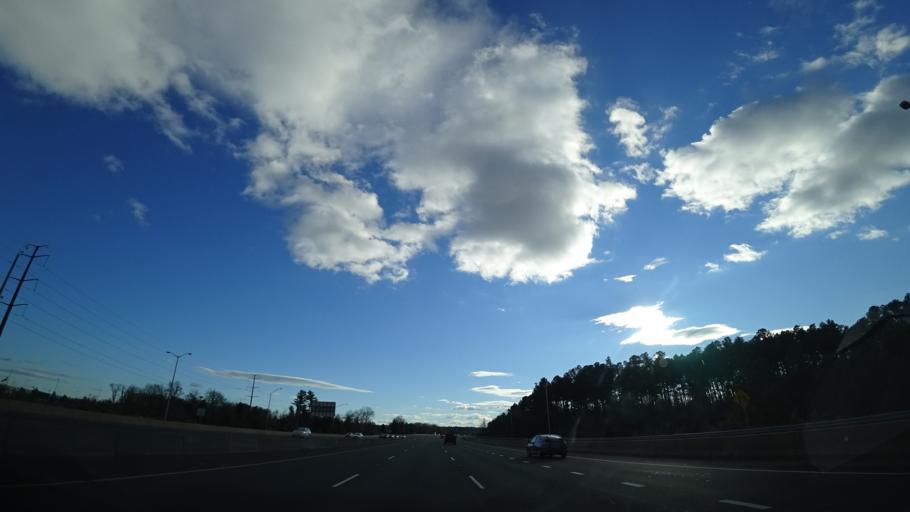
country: US
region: Virginia
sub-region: Fairfax County
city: Chantilly
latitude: 38.9137
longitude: -77.4306
